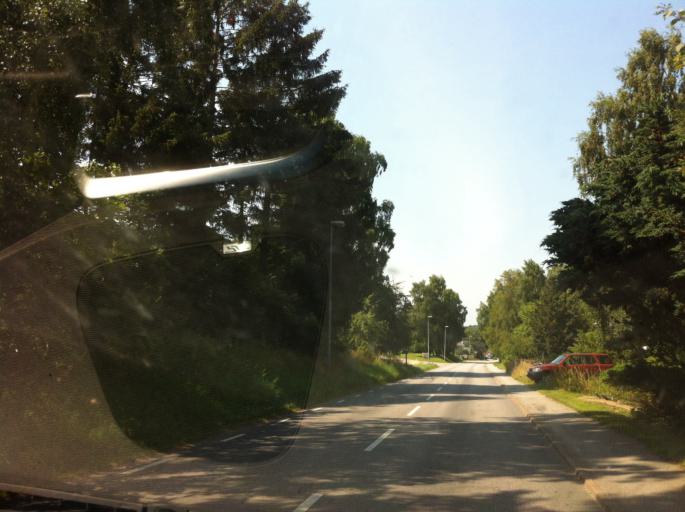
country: SE
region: Skane
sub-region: Hoors Kommun
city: Hoeoer
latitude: 56.0155
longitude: 13.5112
